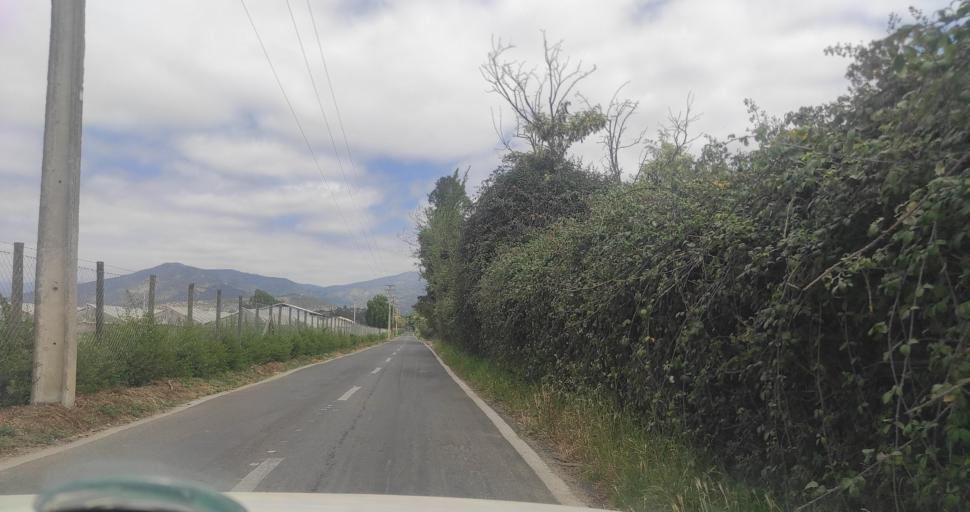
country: CL
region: Valparaiso
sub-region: Provincia de Marga Marga
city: Limache
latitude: -33.0262
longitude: -71.2286
